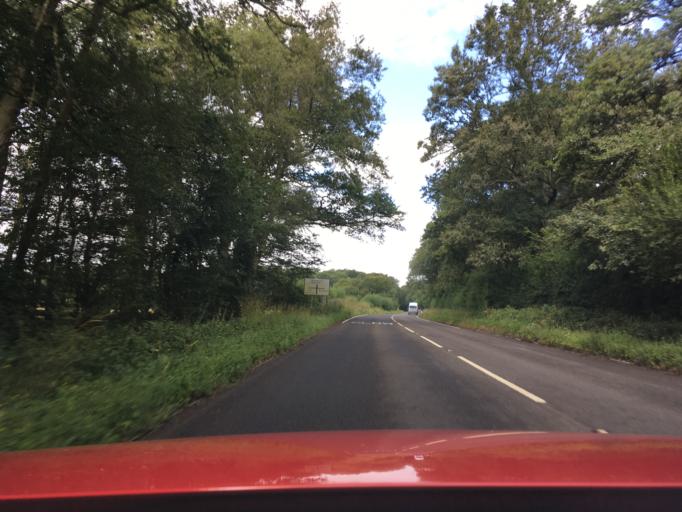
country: GB
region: England
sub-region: West Berkshire
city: Wickham
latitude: 51.4296
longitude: -1.4081
